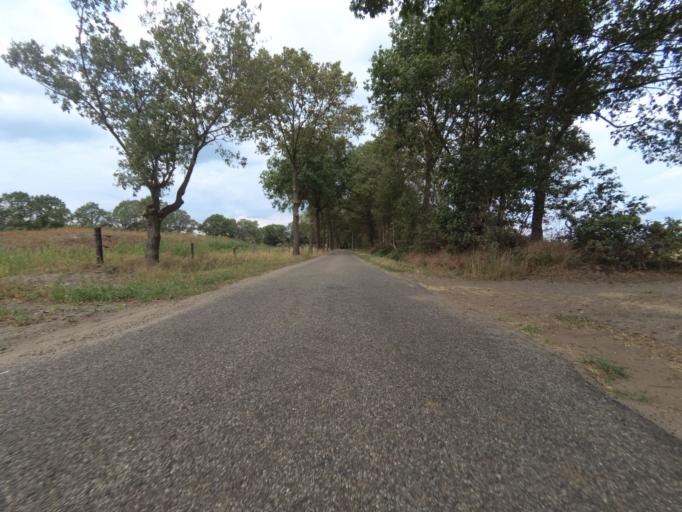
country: NL
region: Overijssel
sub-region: Gemeente Hof van Twente
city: Delden
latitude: 52.2330
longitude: 6.7480
